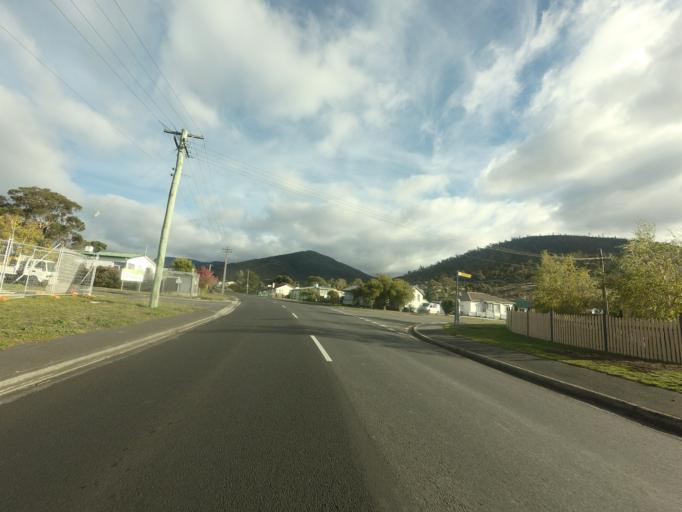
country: AU
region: Tasmania
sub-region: Glenorchy
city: Berriedale
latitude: -42.8046
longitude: 147.2450
